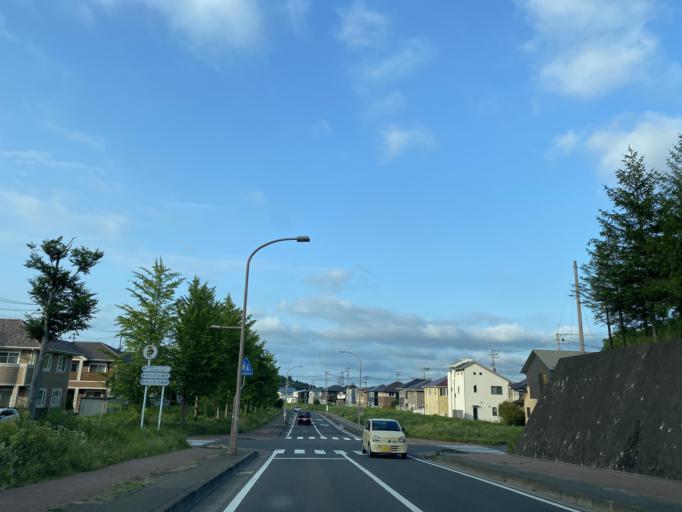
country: JP
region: Miyagi
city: Tomiya
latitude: 38.3830
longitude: 140.8679
